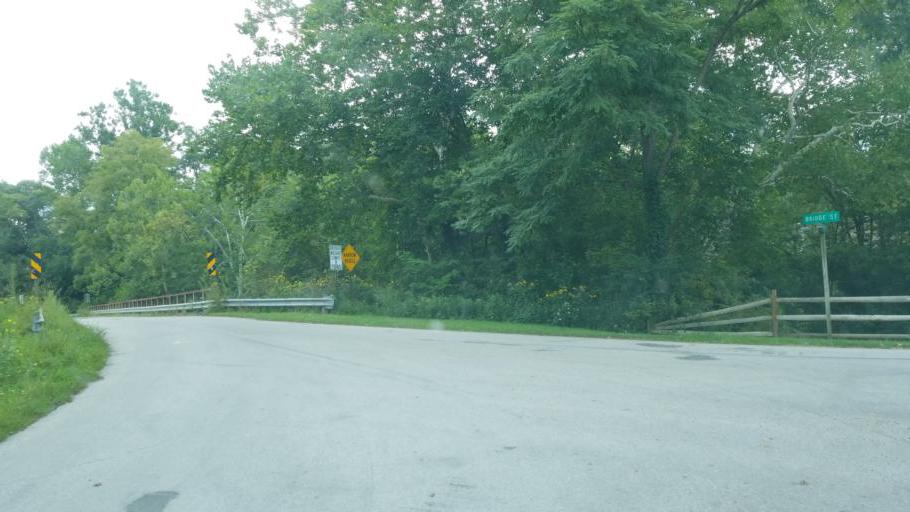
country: US
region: Ohio
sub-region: Knox County
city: Oak Hill
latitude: 40.3966
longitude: -82.2786
